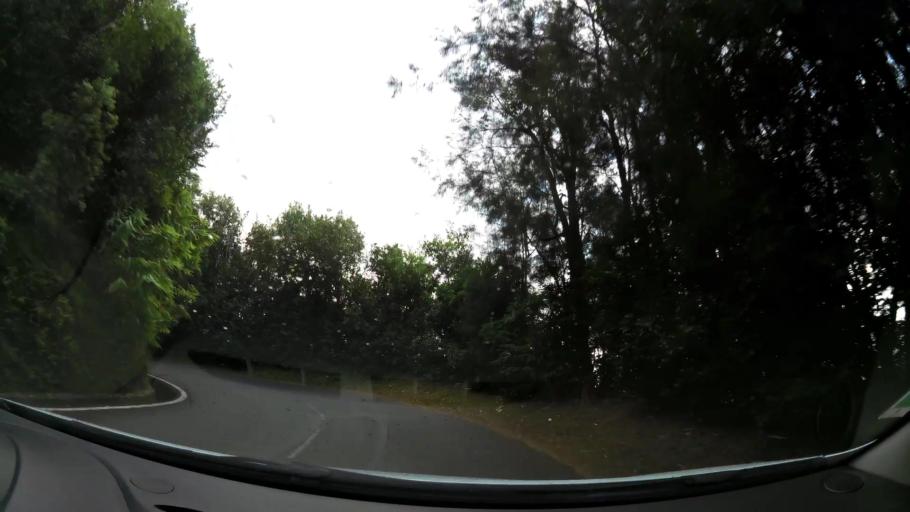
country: RE
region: Reunion
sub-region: Reunion
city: Saint-Denis
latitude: -20.9158
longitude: 55.4398
